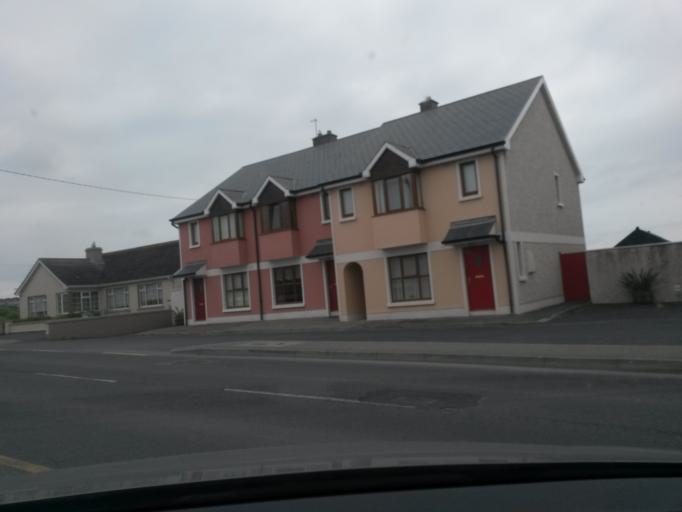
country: IE
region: Munster
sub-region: Ciarrai
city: Ballybunnion
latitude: 52.6749
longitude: -9.6506
